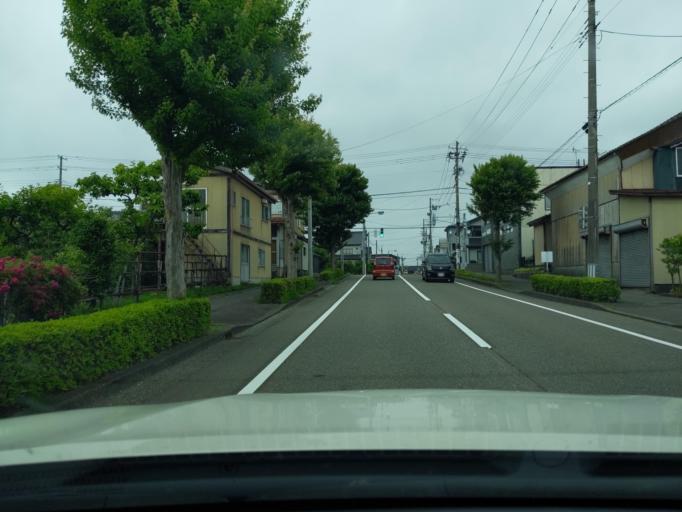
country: JP
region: Niigata
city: Kashiwazaki
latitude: 37.3700
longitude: 138.5674
